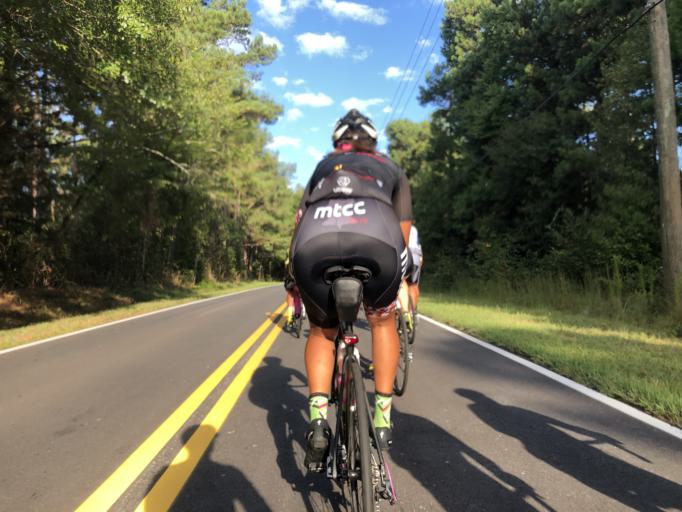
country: US
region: Georgia
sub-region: Fulton County
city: Palmetto
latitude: 33.5770
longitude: -84.6762
